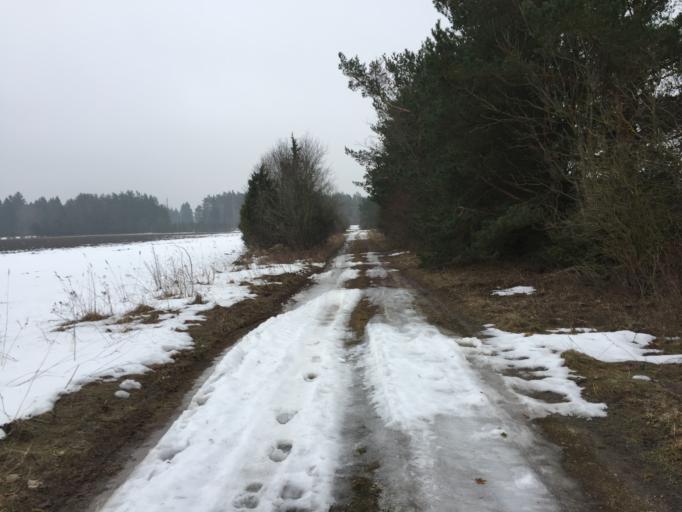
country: EE
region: Saare
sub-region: Orissaare vald
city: Orissaare
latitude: 58.4186
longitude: 22.8212
